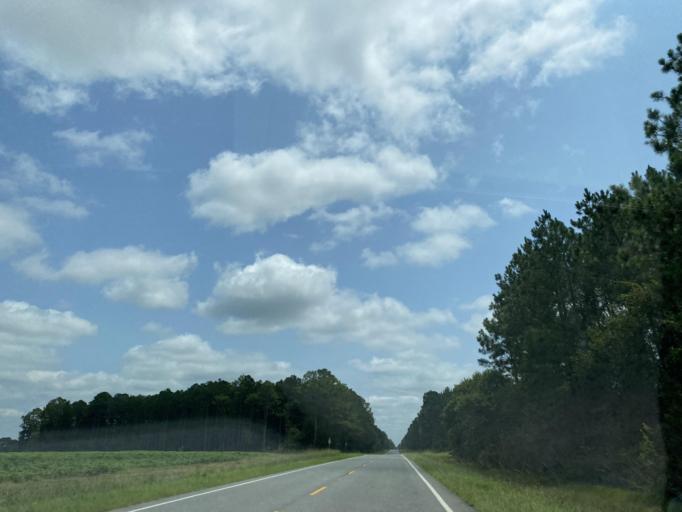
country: US
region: Georgia
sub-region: Bacon County
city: Alma
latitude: 31.7034
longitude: -82.5137
